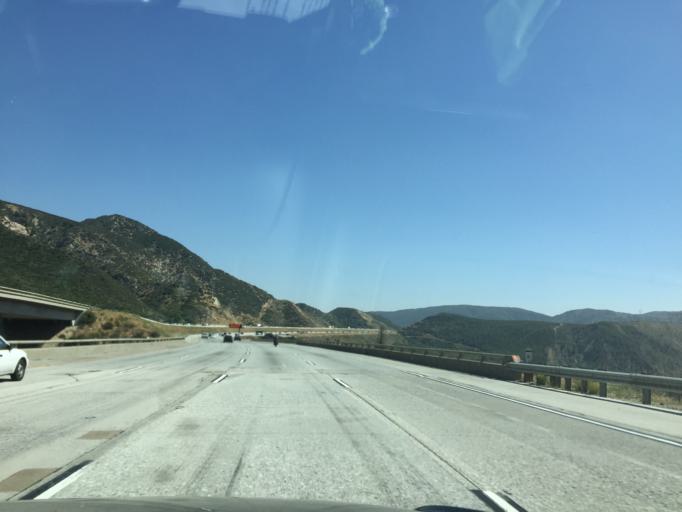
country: US
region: California
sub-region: San Bernardino County
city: Oak Hills
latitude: 34.2788
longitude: -117.4521
